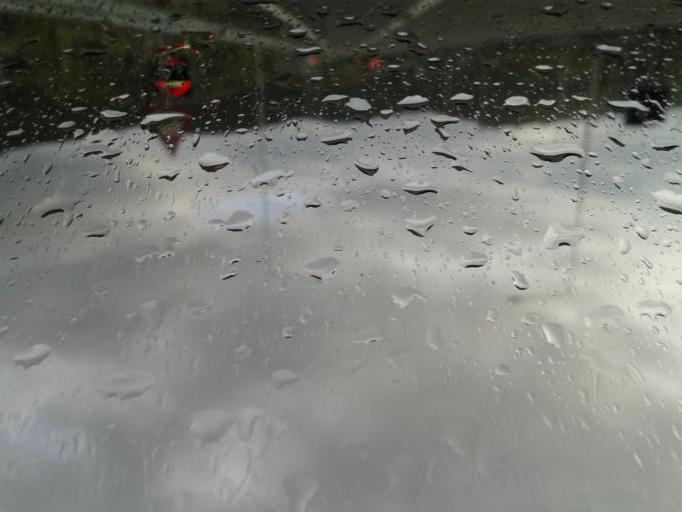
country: GR
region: West Greece
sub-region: Nomos Aitolias kai Akarnanias
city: Galatas
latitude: 38.3849
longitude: 21.5412
